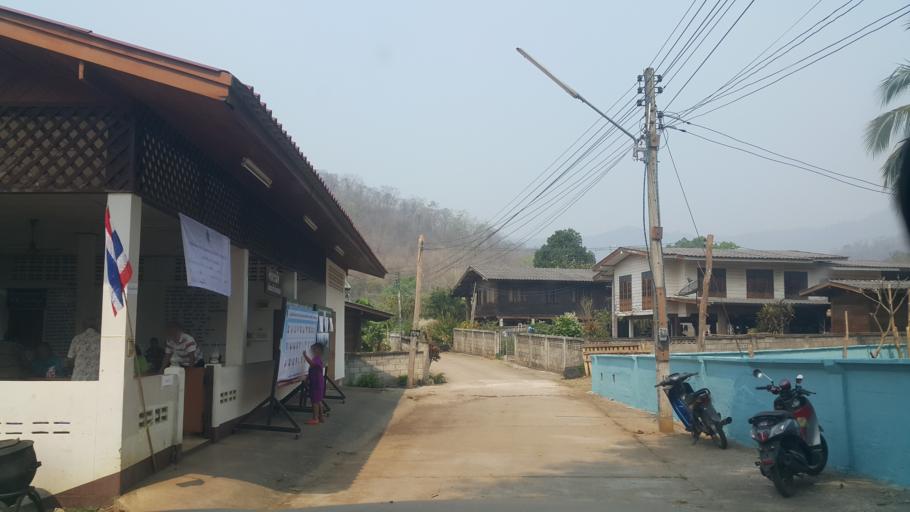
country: TH
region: Lampang
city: Sop Prap
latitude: 17.8046
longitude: 99.2579
